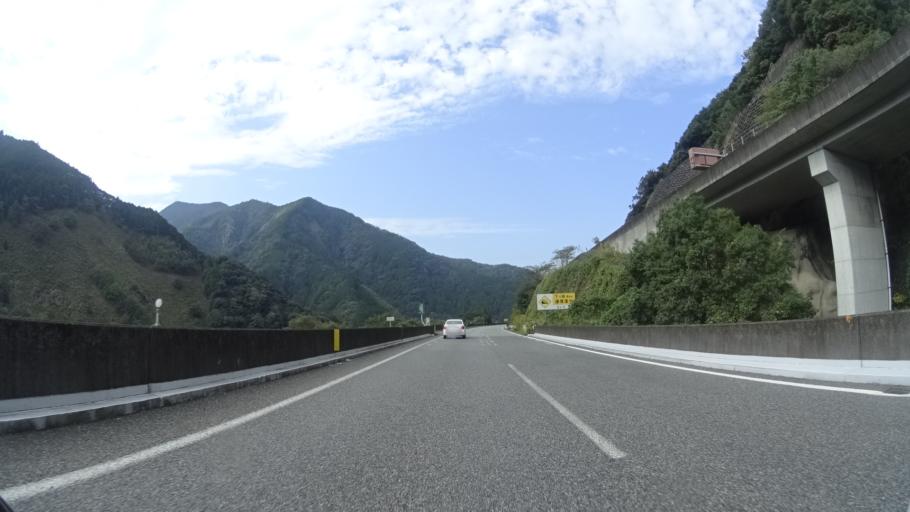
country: JP
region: Kumamoto
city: Yatsushiro
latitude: 32.4351
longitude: 130.6835
